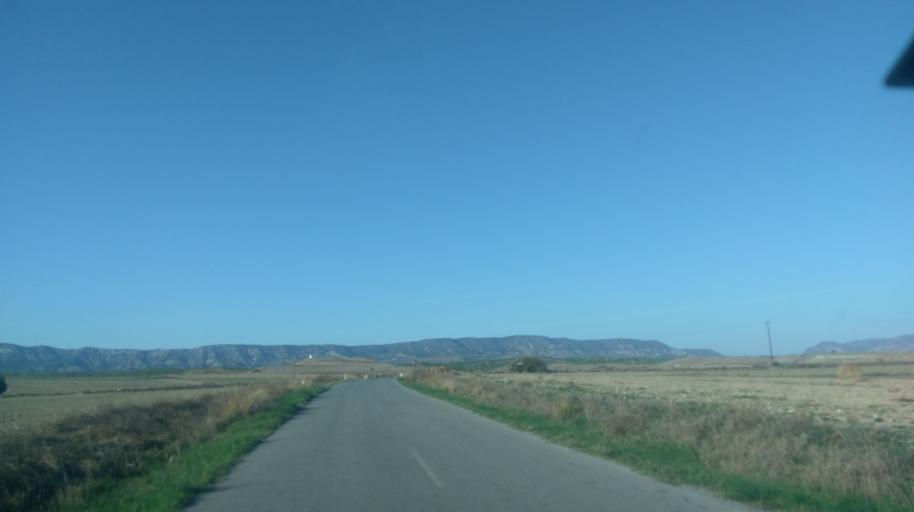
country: CY
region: Ammochostos
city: Lefkonoiko
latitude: 35.2754
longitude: 33.6578
